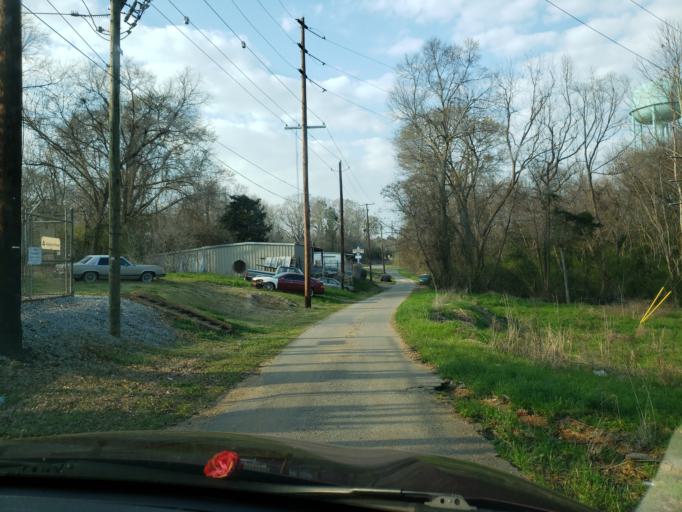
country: US
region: Alabama
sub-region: Hale County
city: Greensboro
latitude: 32.6981
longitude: -87.6067
